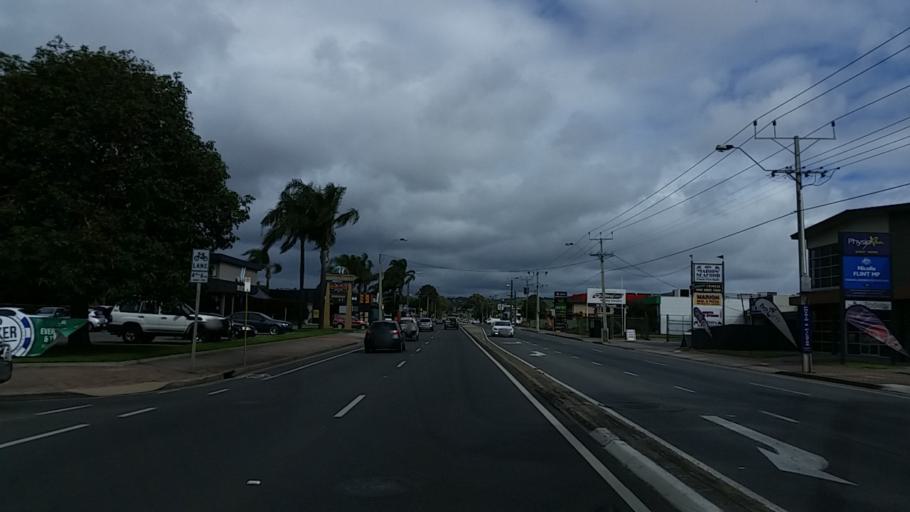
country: AU
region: South Australia
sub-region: Marion
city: Clovelly Park
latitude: -35.0030
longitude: 138.5577
